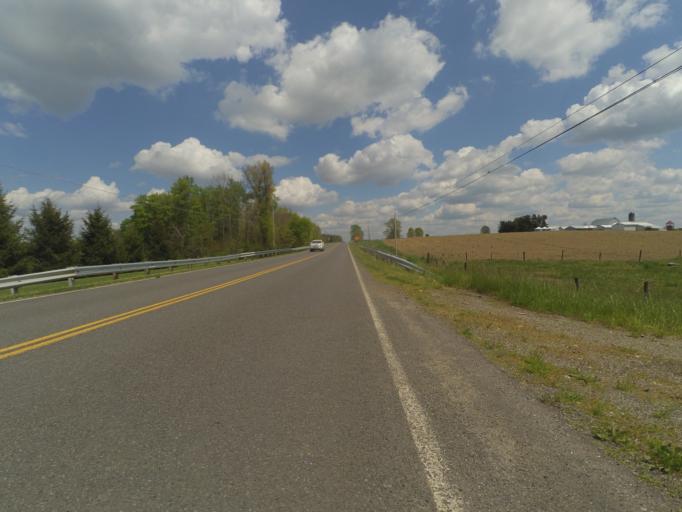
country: US
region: Ohio
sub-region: Mahoning County
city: Craig Beach
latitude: 41.1340
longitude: -81.0549
